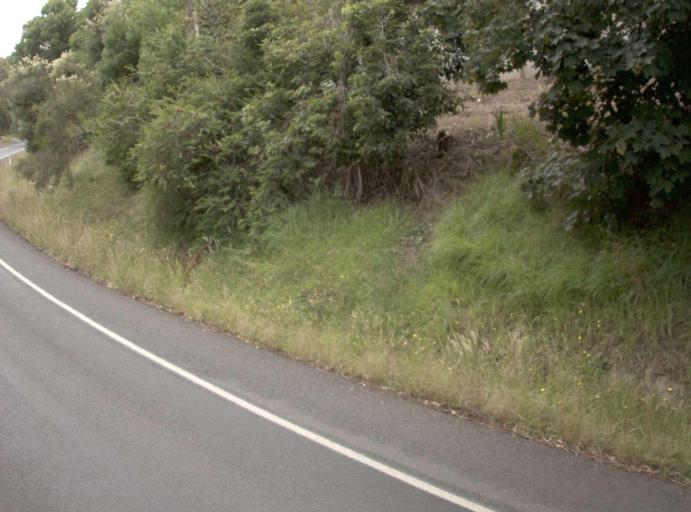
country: AU
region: Victoria
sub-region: Yarra Ranges
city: Healesville
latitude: -37.6467
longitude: 145.5531
